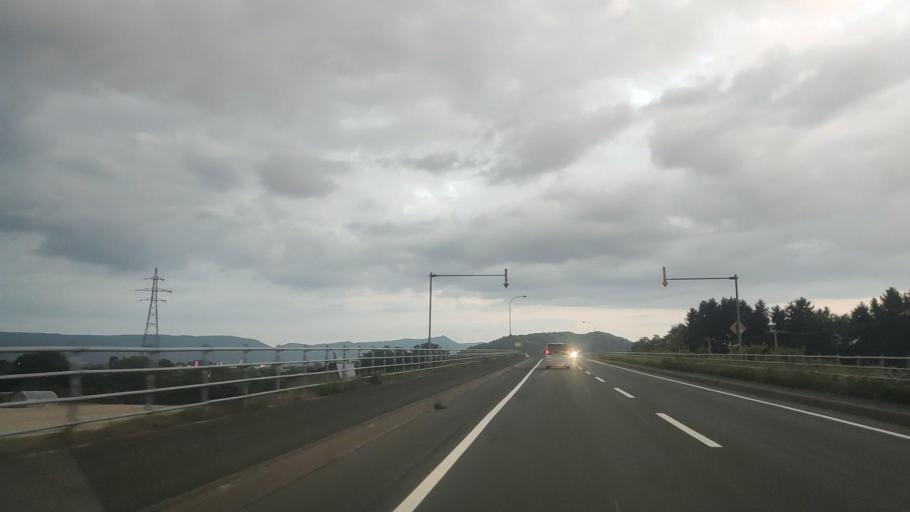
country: JP
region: Hokkaido
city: Shimo-furano
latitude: 43.3548
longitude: 142.3645
